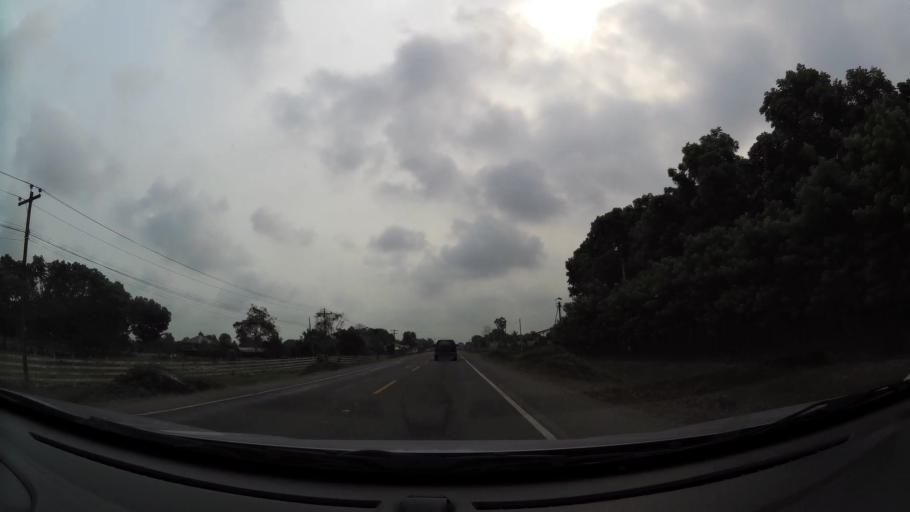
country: HN
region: Yoro
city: Guaimitas
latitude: 15.4863
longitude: -87.7614
